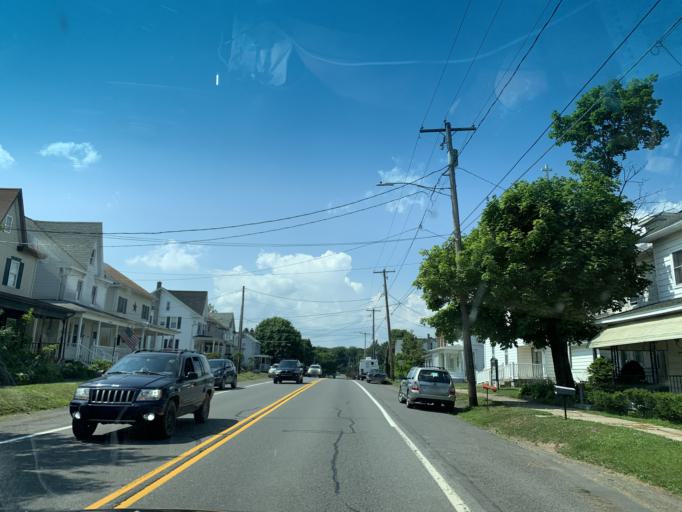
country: US
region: Pennsylvania
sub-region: Schuylkill County
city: Ashland
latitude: 40.8198
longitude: -76.3394
